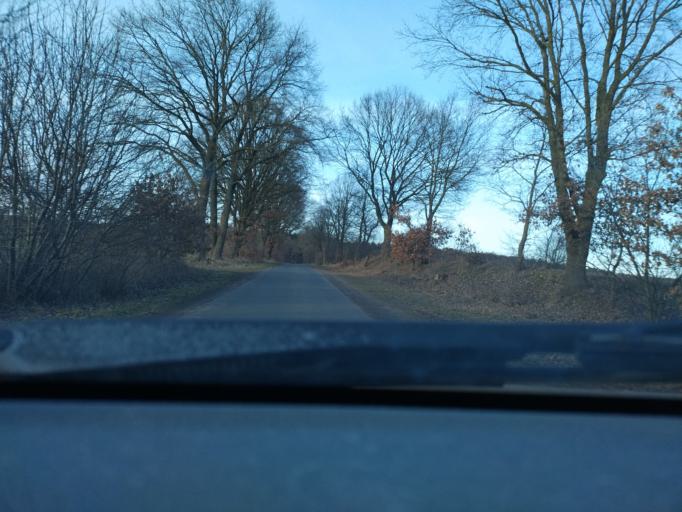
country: DE
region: Schleswig-Holstein
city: Fitzen
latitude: 53.5047
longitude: 10.6505
